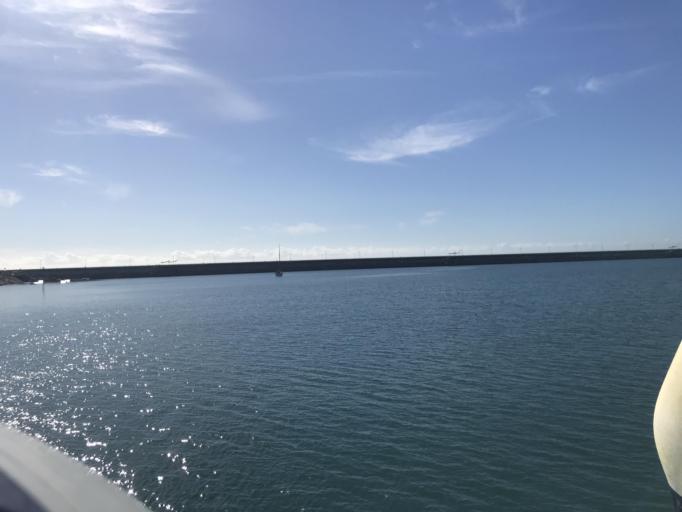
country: ES
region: Valencia
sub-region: Provincia de Alicante
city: Torrevieja
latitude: 37.9708
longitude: -0.6857
